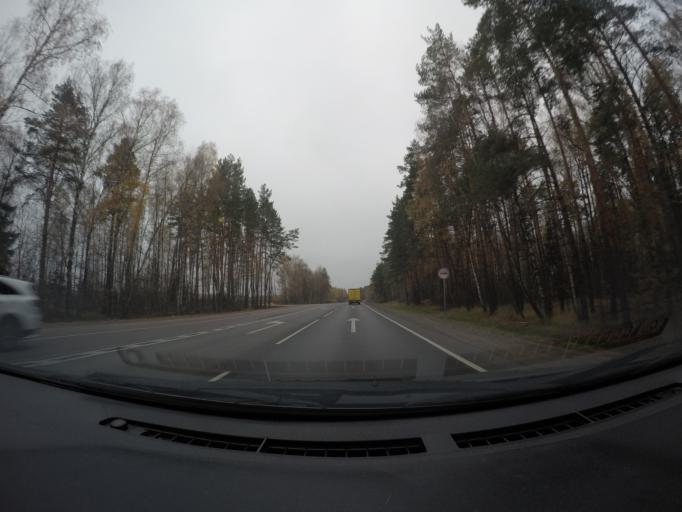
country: RU
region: Moskovskaya
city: Malyshevo
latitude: 55.5267
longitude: 38.3968
